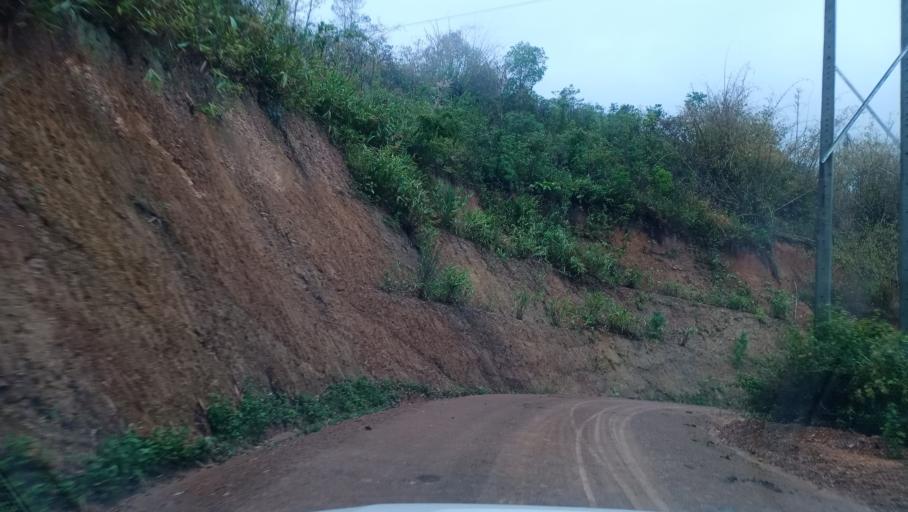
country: LA
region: Phongsali
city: Khoa
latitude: 21.3111
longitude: 102.7014
